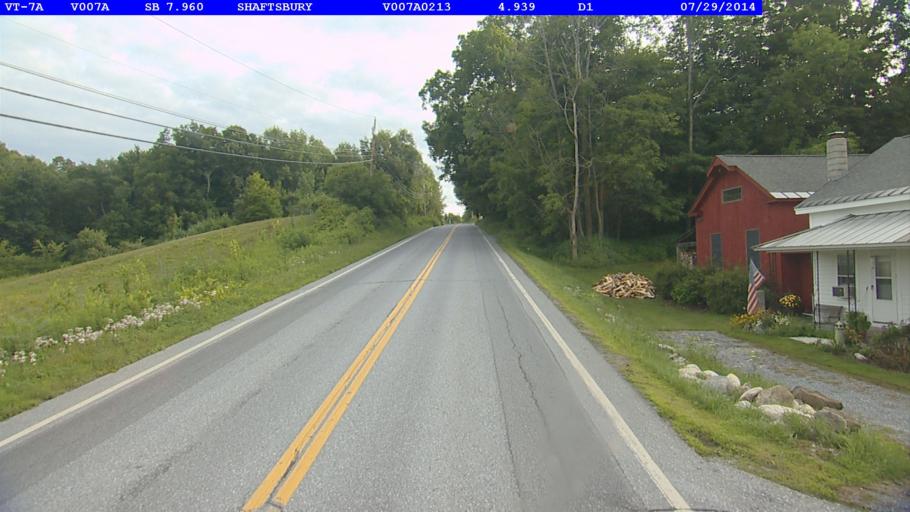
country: US
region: Vermont
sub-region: Bennington County
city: North Bennington
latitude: 43.0019
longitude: -73.1977
